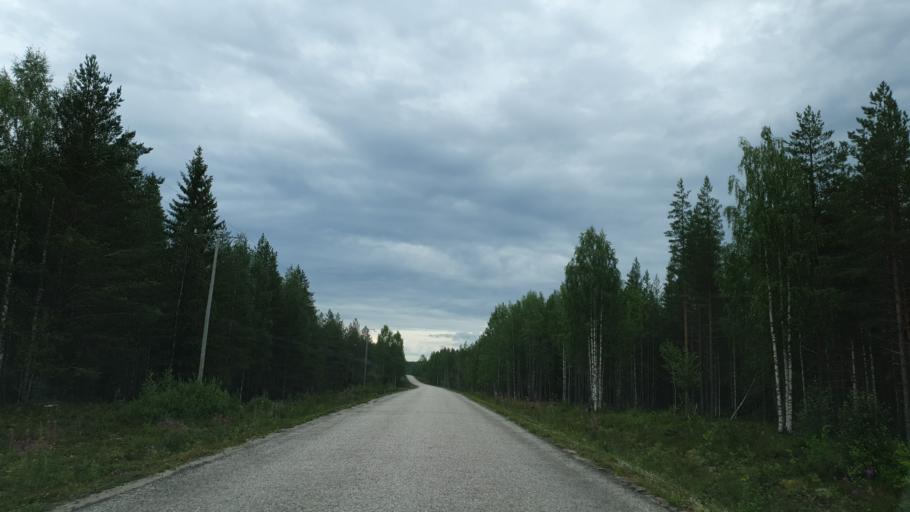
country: FI
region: Kainuu
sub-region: Kehys-Kainuu
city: Kuhmo
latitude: 64.3421
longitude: 29.3024
